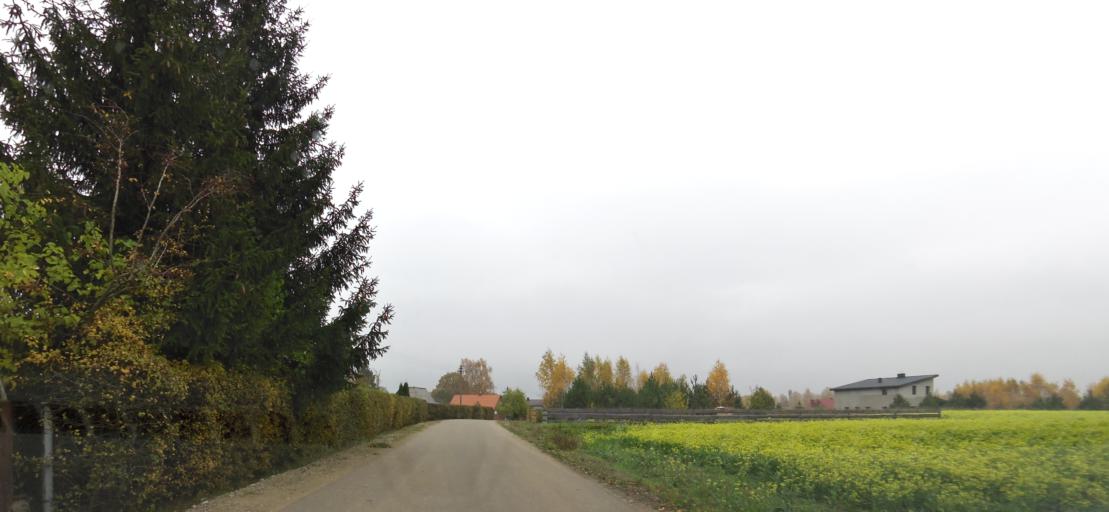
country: LT
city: Skaidiskes
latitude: 54.6429
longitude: 25.6200
